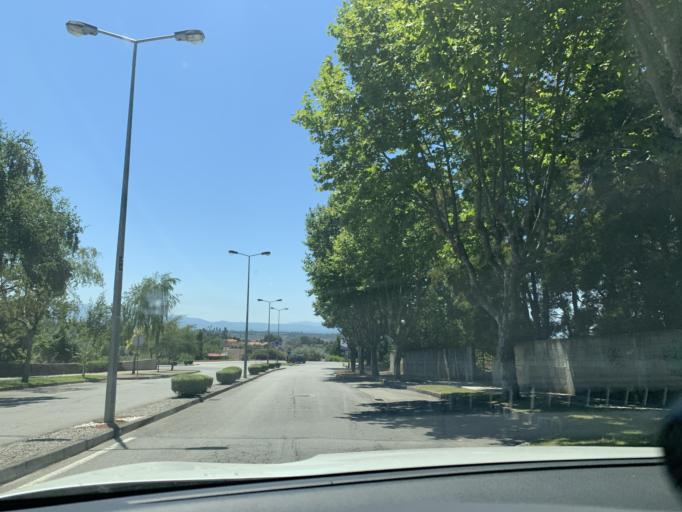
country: PT
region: Viseu
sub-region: Mangualde
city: Mangualde
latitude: 40.6005
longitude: -7.7618
